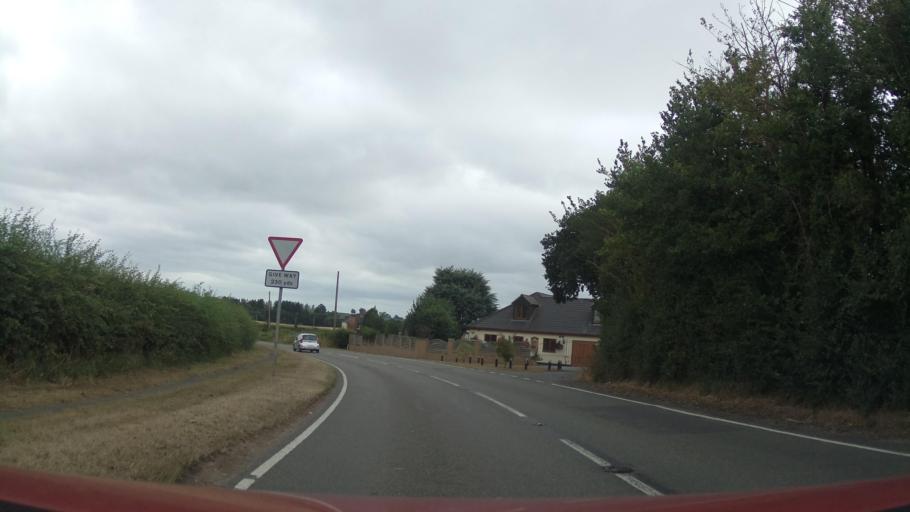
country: GB
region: England
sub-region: Leicestershire
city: Donisthorpe
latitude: 52.7156
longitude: -1.5523
